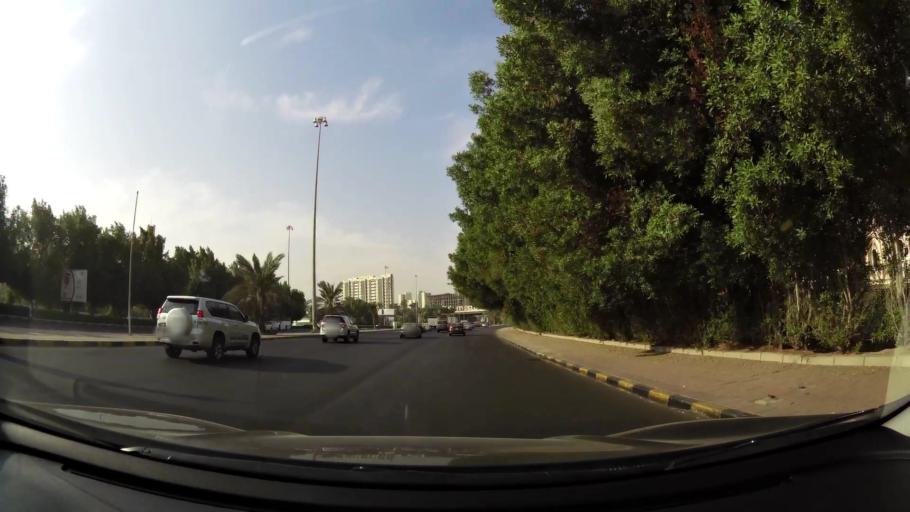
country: KW
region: Muhafazat Hawalli
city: Salwa
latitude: 29.2708
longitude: 48.0875
